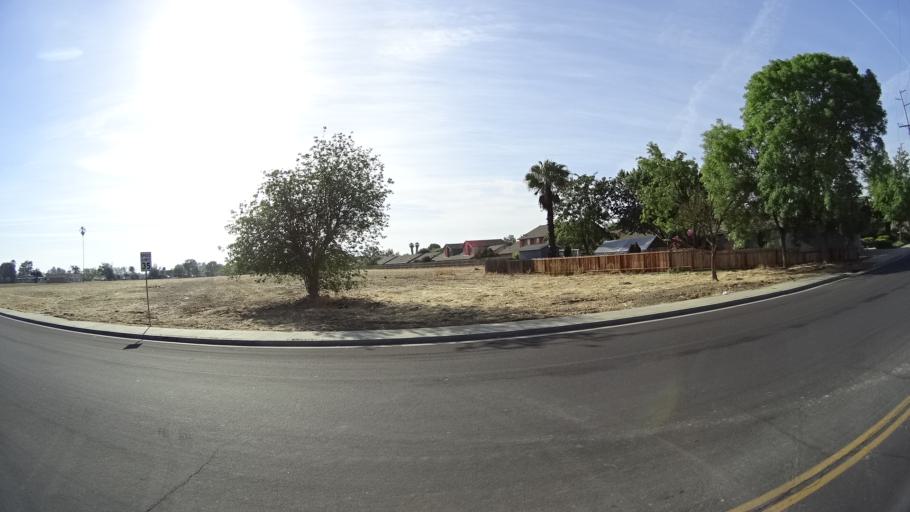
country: US
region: California
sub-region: Kings County
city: Hanford
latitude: 36.3170
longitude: -119.6458
